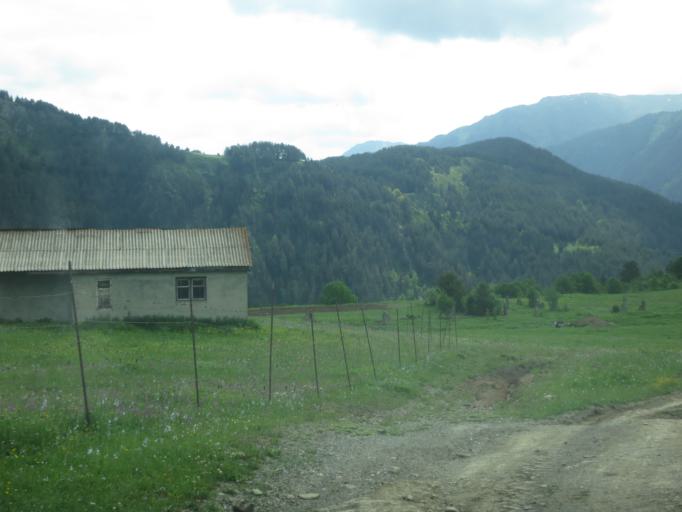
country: RU
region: Chechnya
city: Itum-Kali
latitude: 42.3682
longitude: 45.6376
